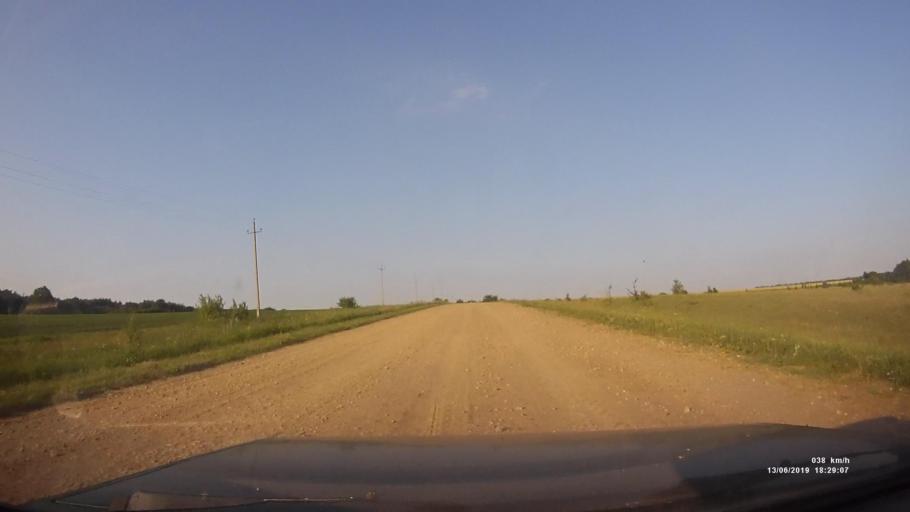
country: RU
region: Rostov
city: Kazanskaya
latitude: 49.8584
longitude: 41.3382
